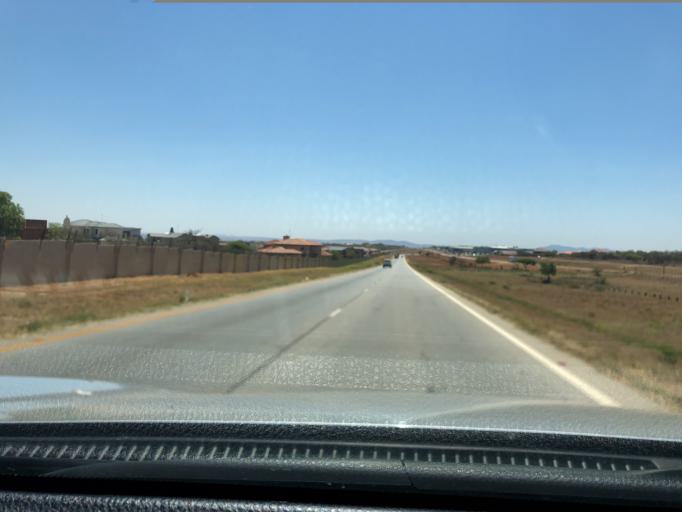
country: ZA
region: Limpopo
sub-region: Capricorn District Municipality
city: Polokwane
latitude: -23.8888
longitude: 29.5080
